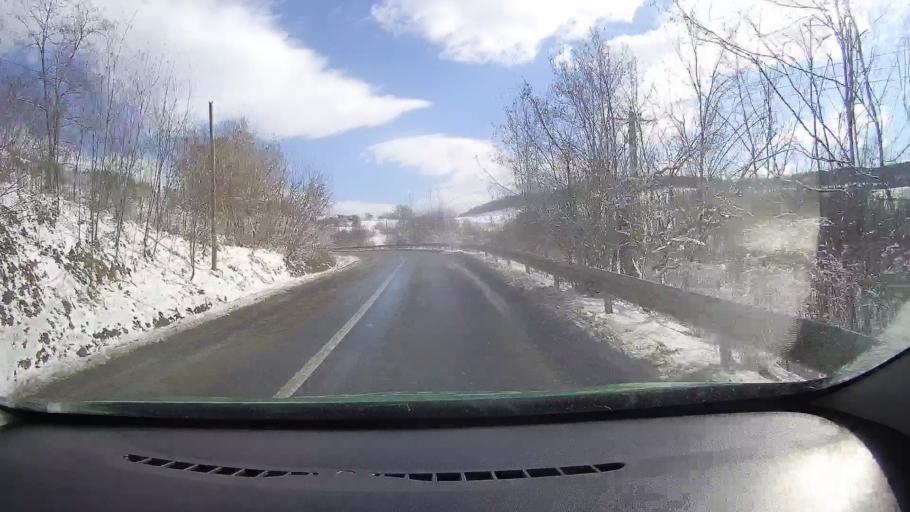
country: RO
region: Sibiu
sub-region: Comuna Barghis
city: Barghis
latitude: 45.9837
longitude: 24.5071
